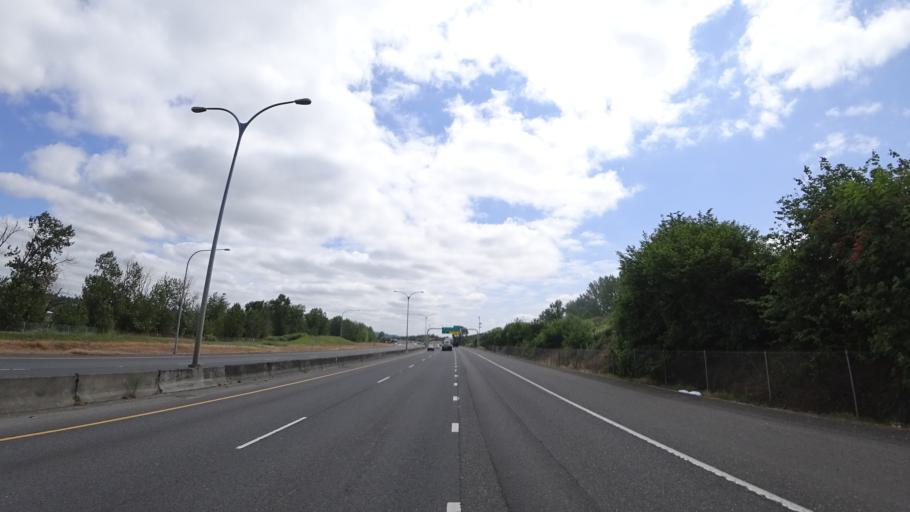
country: US
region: Washington
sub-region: Clark County
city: Vancouver
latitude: 45.6191
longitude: -122.6617
